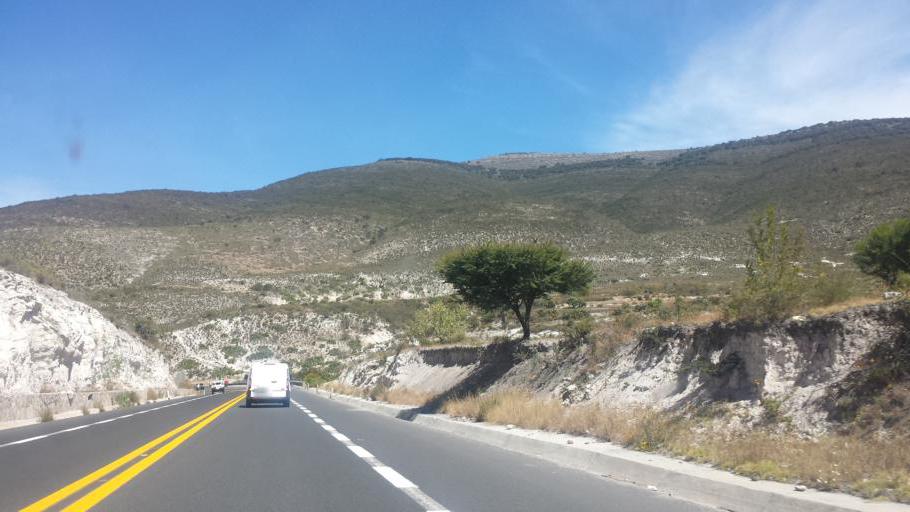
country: MX
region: Oaxaca
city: San Gabriel Casa Blanca
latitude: 17.9815
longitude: -97.3544
